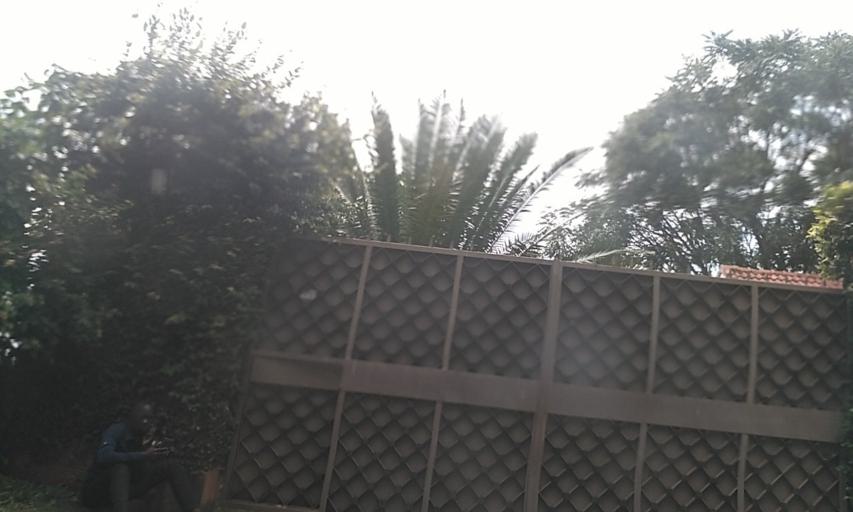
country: UG
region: Central Region
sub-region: Kampala District
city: Kampala
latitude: 0.3315
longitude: 32.5942
